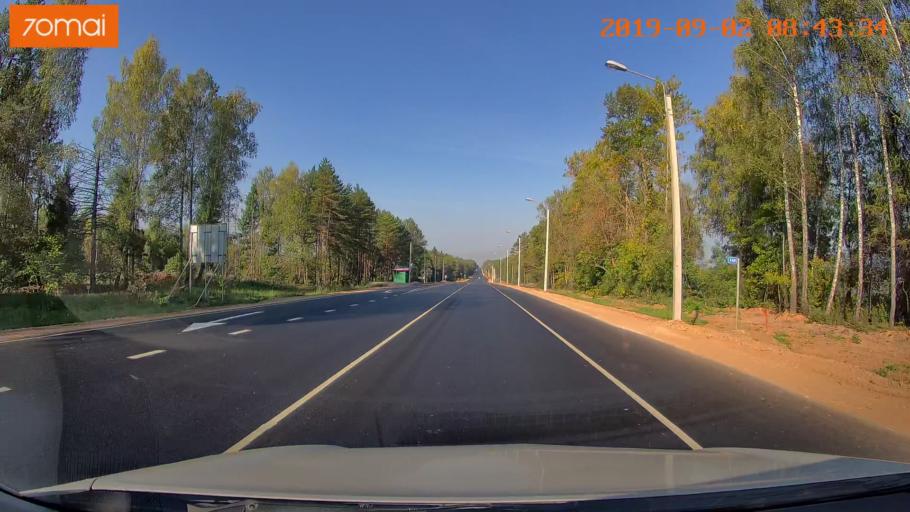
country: RU
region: Kaluga
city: Kudinovo
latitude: 54.9714
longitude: 36.0571
